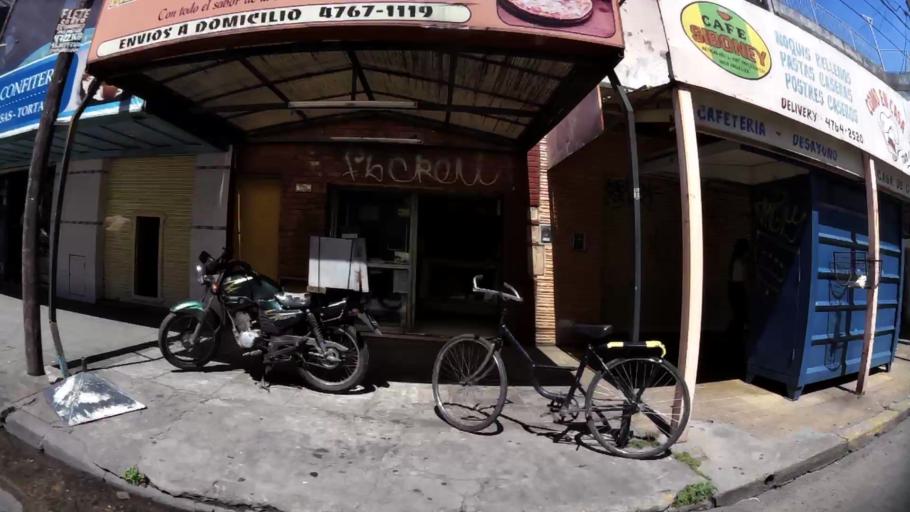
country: AR
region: Buenos Aires
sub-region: Partido de General San Martin
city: General San Martin
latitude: -34.5669
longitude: -58.5513
